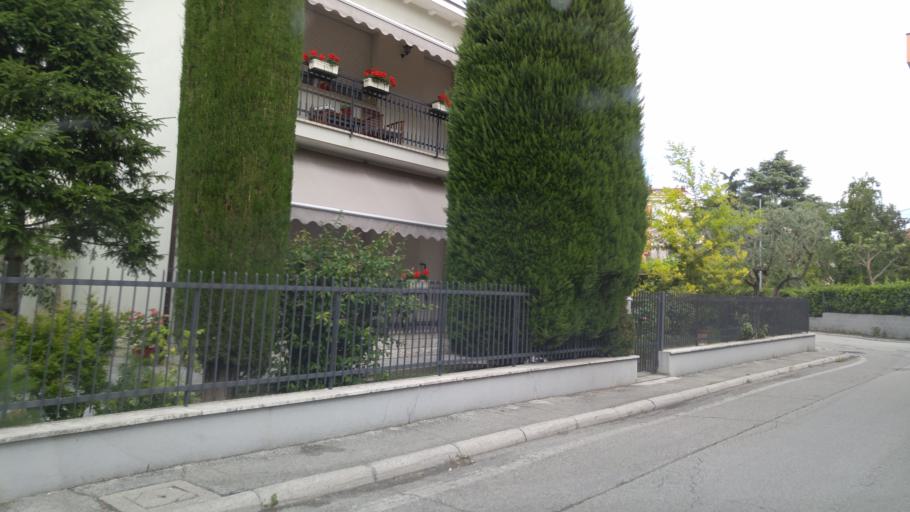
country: IT
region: Emilia-Romagna
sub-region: Provincia di Rimini
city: Rimini
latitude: 44.0460
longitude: 12.5743
